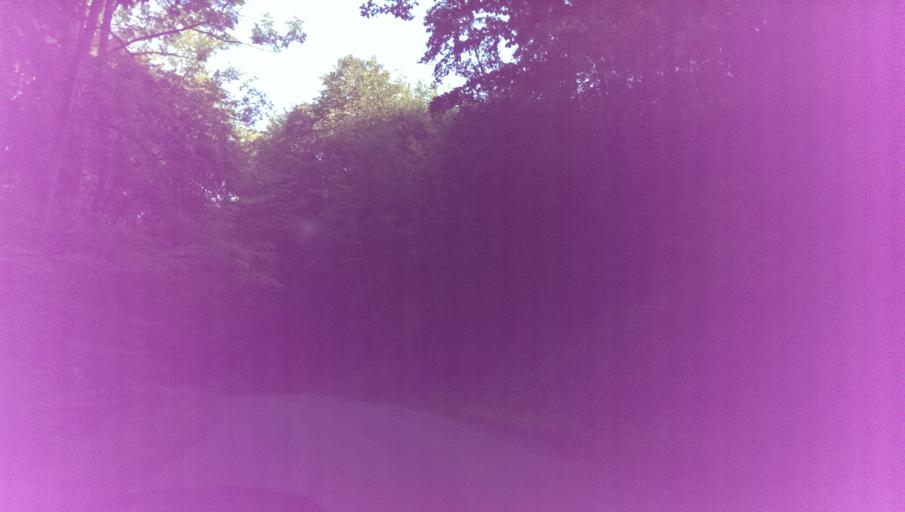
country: CZ
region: Zlin
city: Korycany
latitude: 49.0938
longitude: 17.1786
